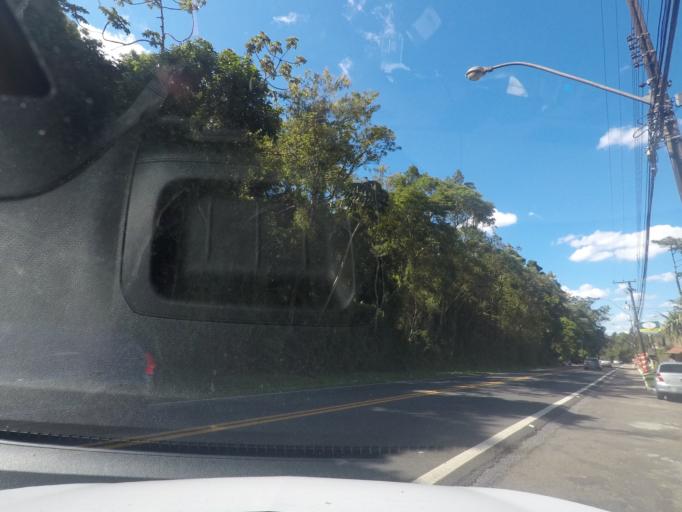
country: BR
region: Rio de Janeiro
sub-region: Teresopolis
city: Teresopolis
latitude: -22.4548
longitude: -42.9839
